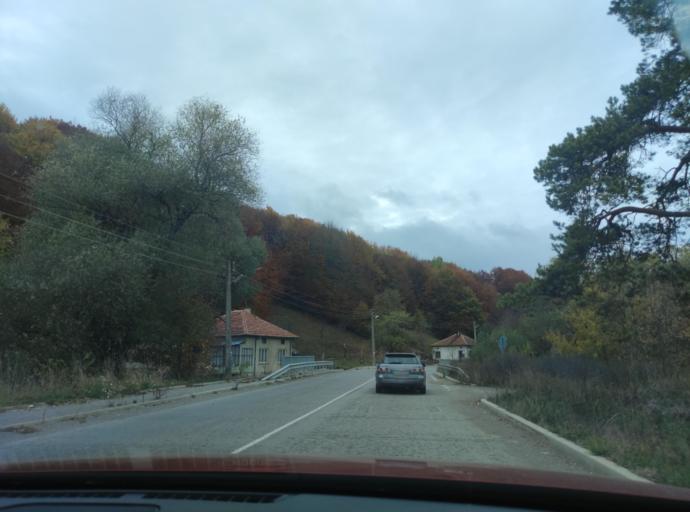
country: BG
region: Sofiya
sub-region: Obshtina Godech
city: Godech
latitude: 43.0816
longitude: 23.1050
